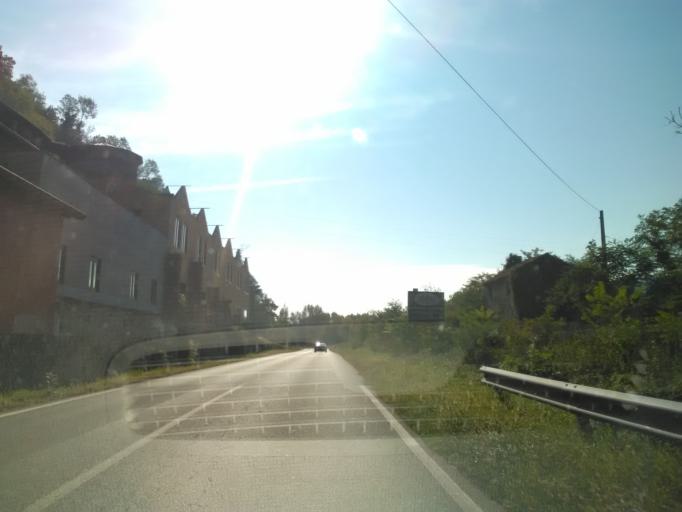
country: IT
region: Piedmont
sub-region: Provincia di Vercelli
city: Serravalle Sesia
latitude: 45.7006
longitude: 8.3065
